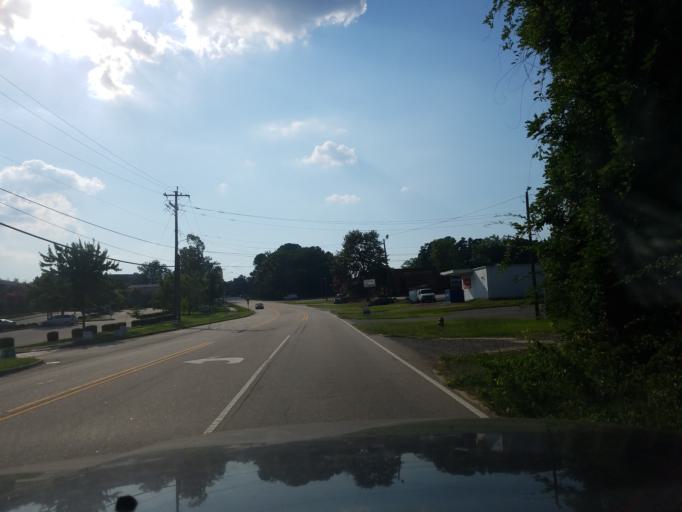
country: US
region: North Carolina
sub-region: Durham County
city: Durham
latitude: 35.9731
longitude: -78.9328
